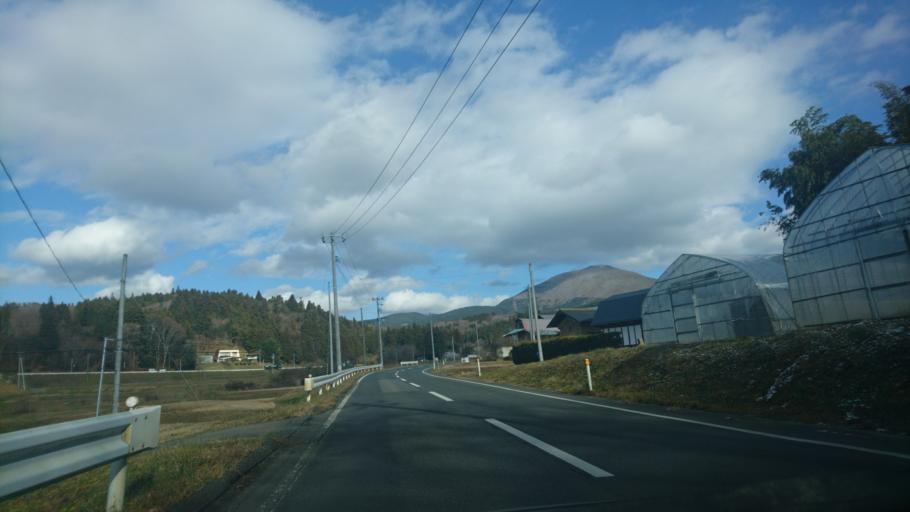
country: JP
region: Iwate
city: Ichinoseki
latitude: 38.9499
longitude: 141.4088
